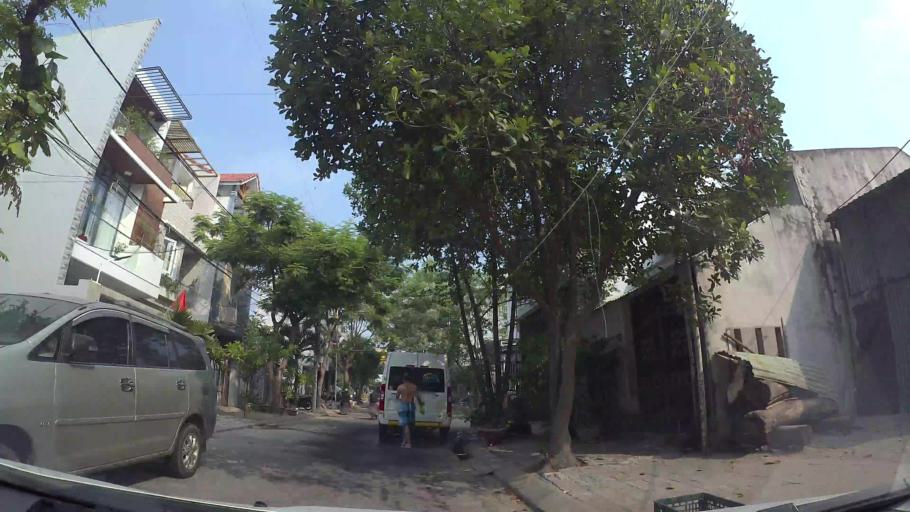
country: VN
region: Da Nang
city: Ngu Hanh Son
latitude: 16.0310
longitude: 108.2460
